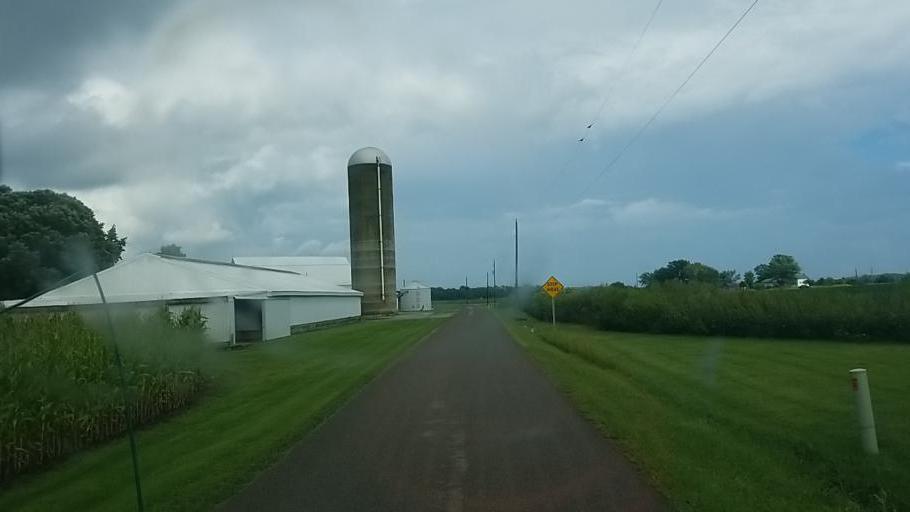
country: US
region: Ohio
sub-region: Hardin County
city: Kenton
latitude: 40.5170
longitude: -83.5106
